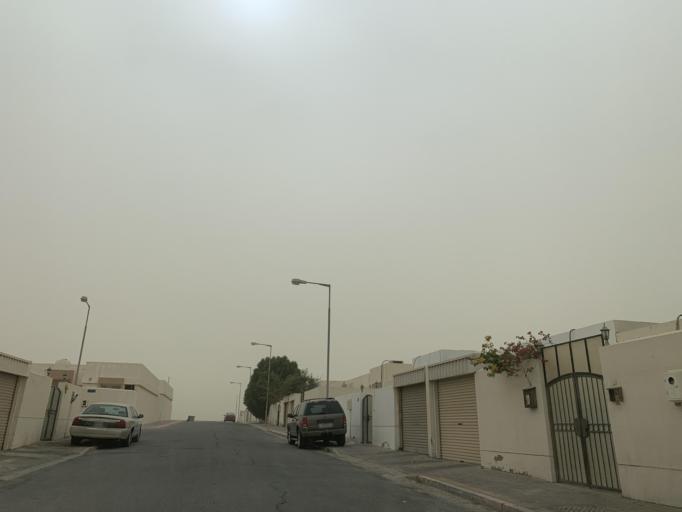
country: BH
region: Central Governorate
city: Madinat Hamad
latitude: 26.1337
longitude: 50.5207
